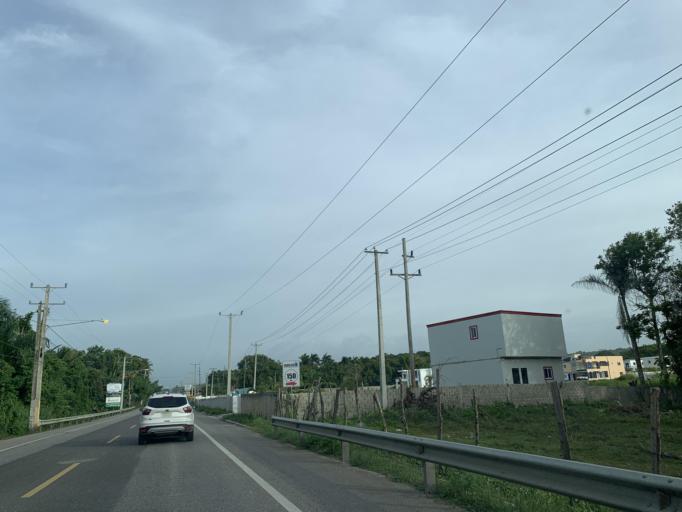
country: DO
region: Puerto Plata
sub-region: Puerto Plata
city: Puerto Plata
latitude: 19.7513
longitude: -70.6405
